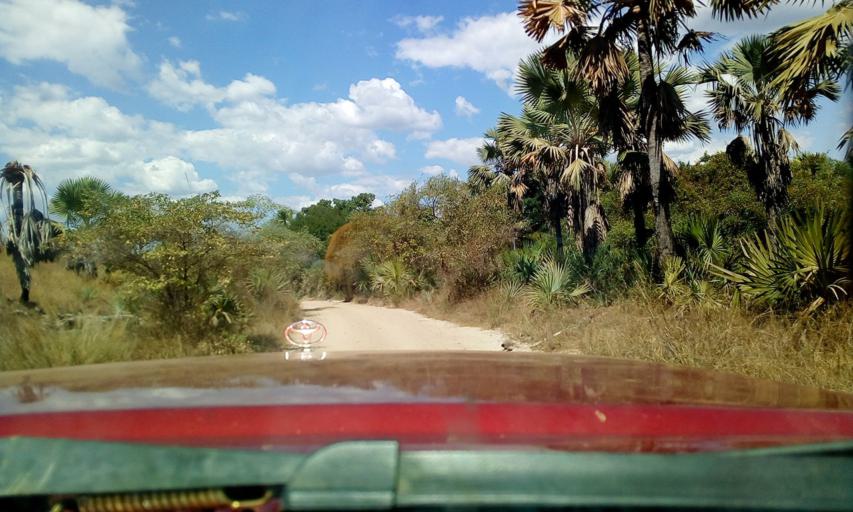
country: MG
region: Boeny
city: Sitampiky
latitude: -16.1300
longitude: 45.4952
